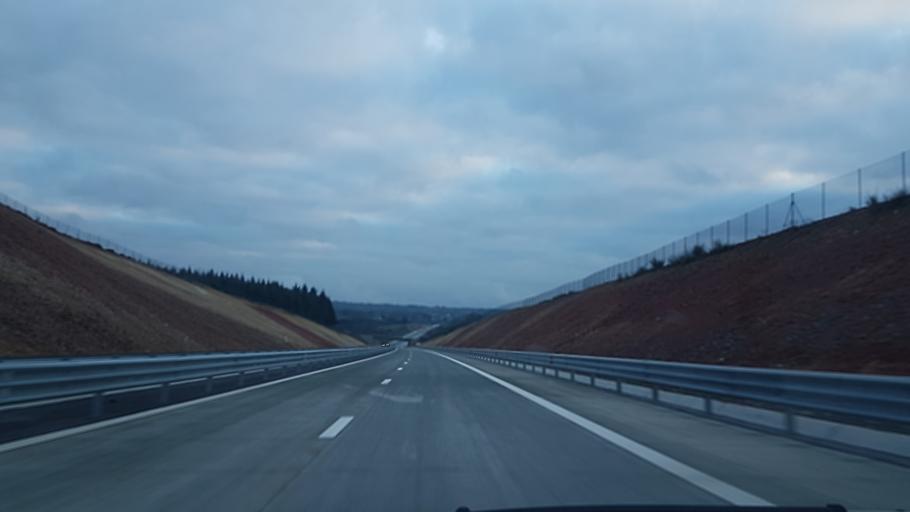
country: FR
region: Champagne-Ardenne
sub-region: Departement des Ardennes
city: Rocroi
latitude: 49.9833
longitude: 4.5394
